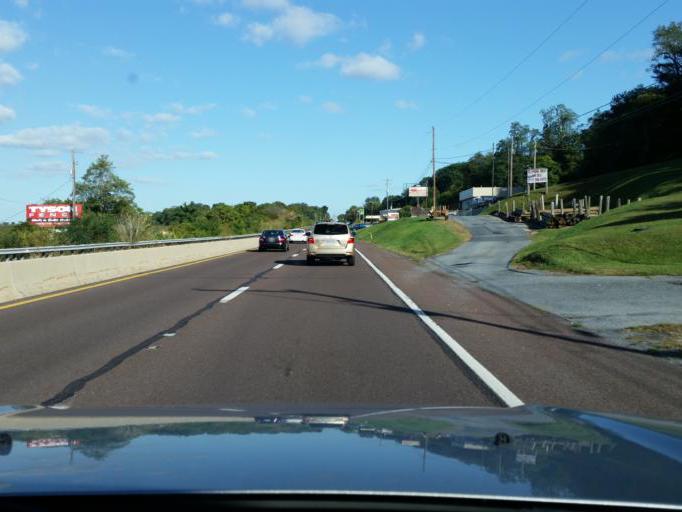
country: US
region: Pennsylvania
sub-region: Dauphin County
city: Rutherford
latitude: 40.2619
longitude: -76.7525
